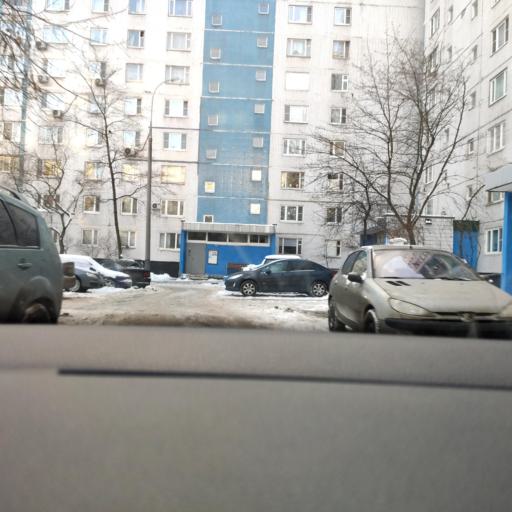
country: RU
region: Moscow
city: Kolomenskoye
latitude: 55.6803
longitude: 37.7020
